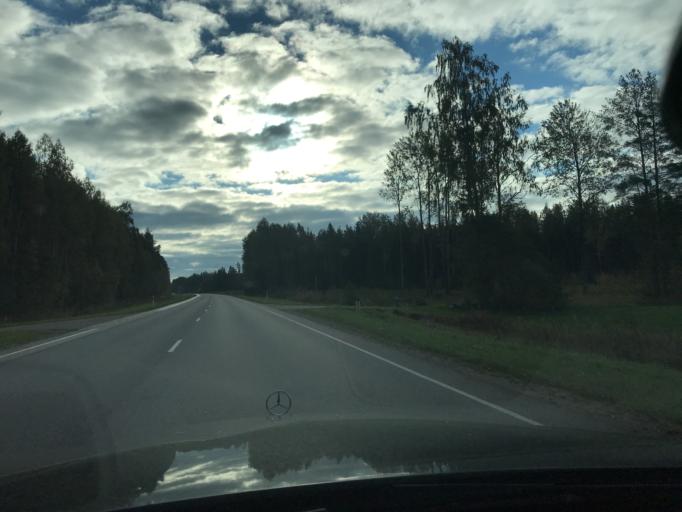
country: EE
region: Paernumaa
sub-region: Saarde vald
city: Kilingi-Nomme
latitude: 58.1675
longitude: 24.8228
